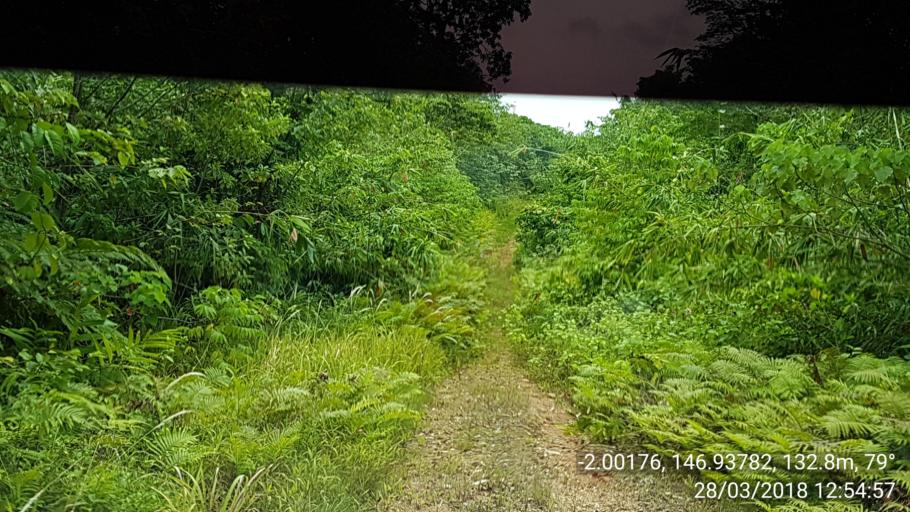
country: PG
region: Manus
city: Lorengau
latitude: -2.0017
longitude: 146.9378
